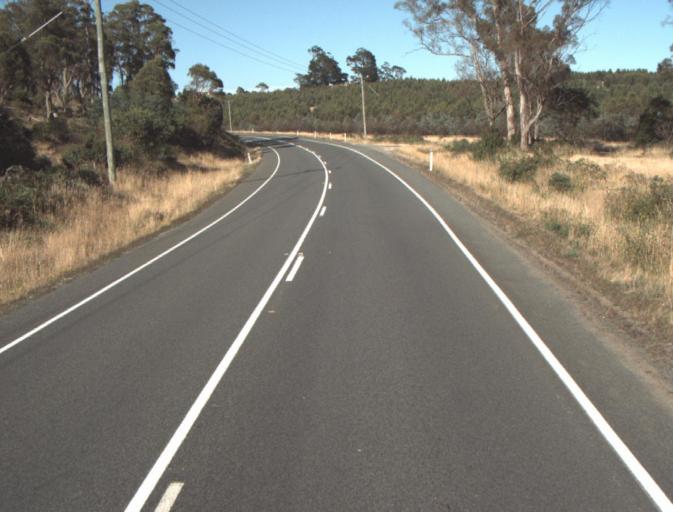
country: AU
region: Tasmania
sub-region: Launceston
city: Newstead
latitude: -41.4047
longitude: 147.2834
